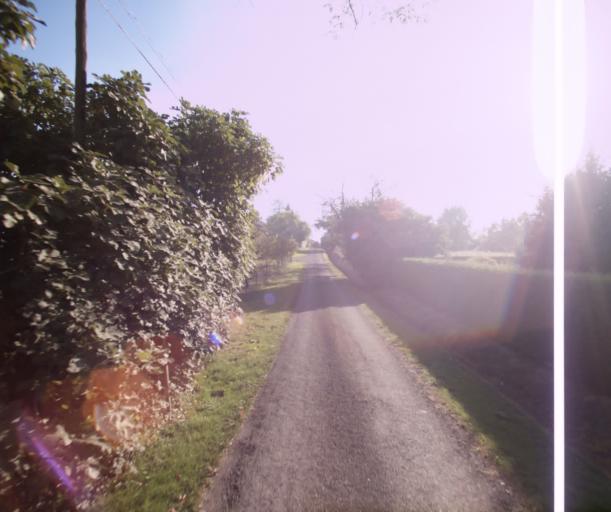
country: FR
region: Midi-Pyrenees
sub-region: Departement du Gers
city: Eauze
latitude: 43.8721
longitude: 0.0464
